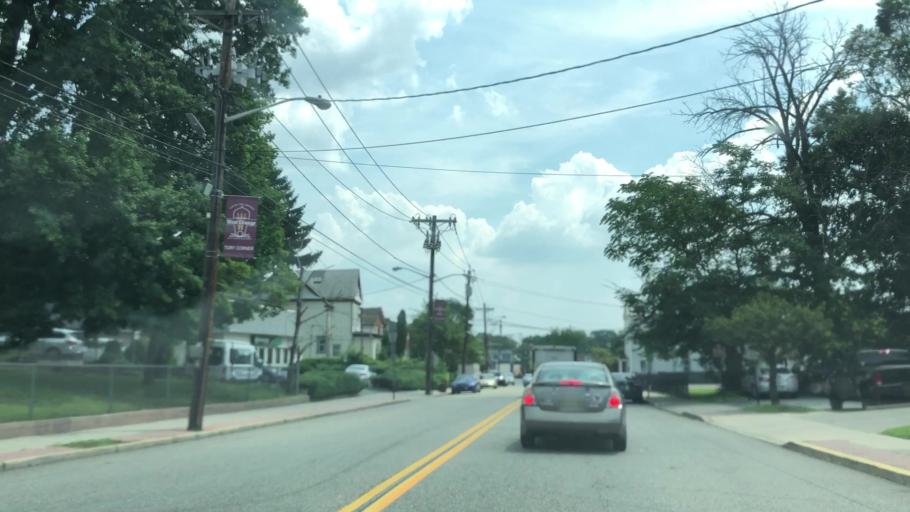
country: US
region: New Jersey
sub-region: Essex County
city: West Orange
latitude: 40.7871
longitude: -74.2307
